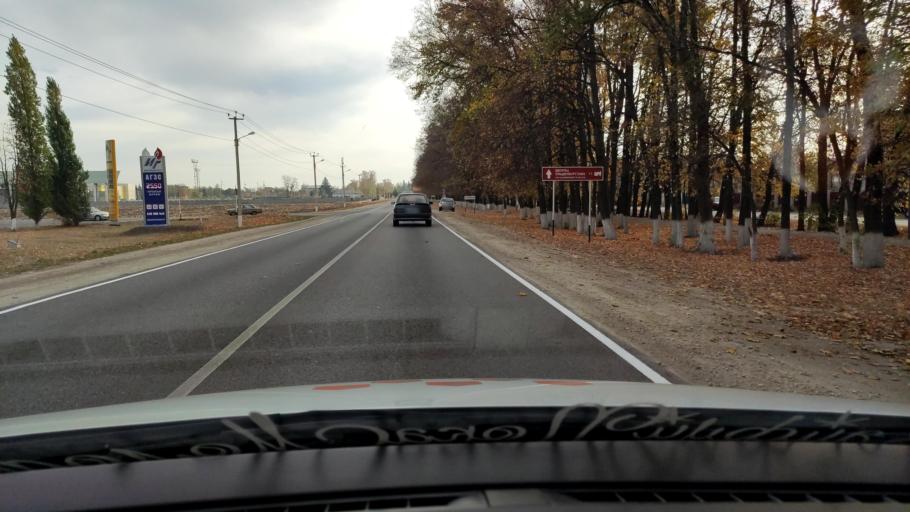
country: RU
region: Voronezj
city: Ramon'
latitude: 51.9125
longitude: 39.3216
